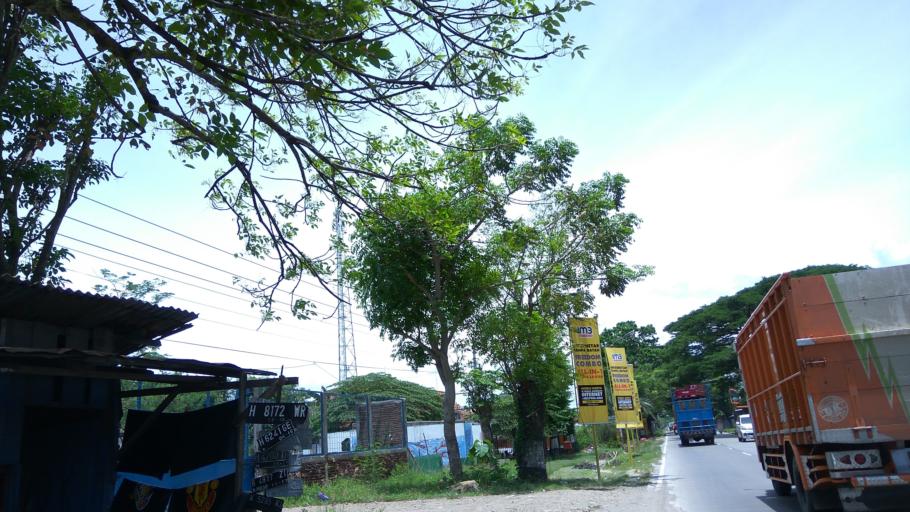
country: ID
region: Central Java
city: Mranggen
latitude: -7.0458
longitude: 110.5820
